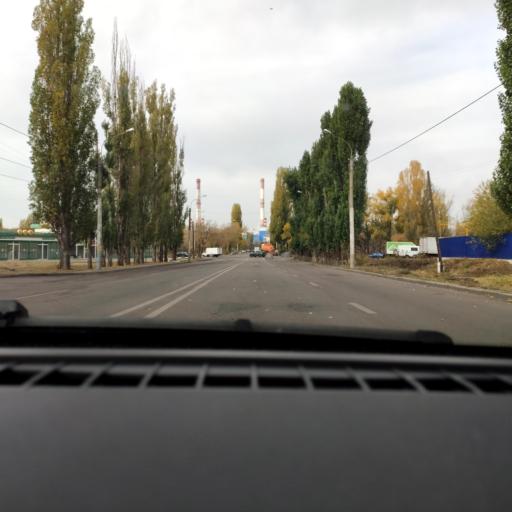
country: RU
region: Voronezj
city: Maslovka
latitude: 51.6225
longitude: 39.2389
